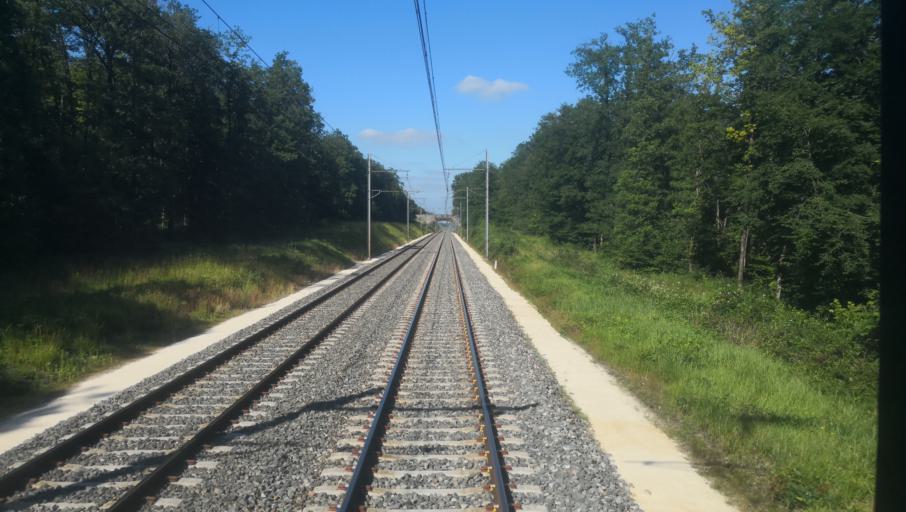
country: FR
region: Ile-de-France
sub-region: Departement de Seine-et-Marne
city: Montigny-sur-Loing
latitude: 48.3481
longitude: 2.7763
